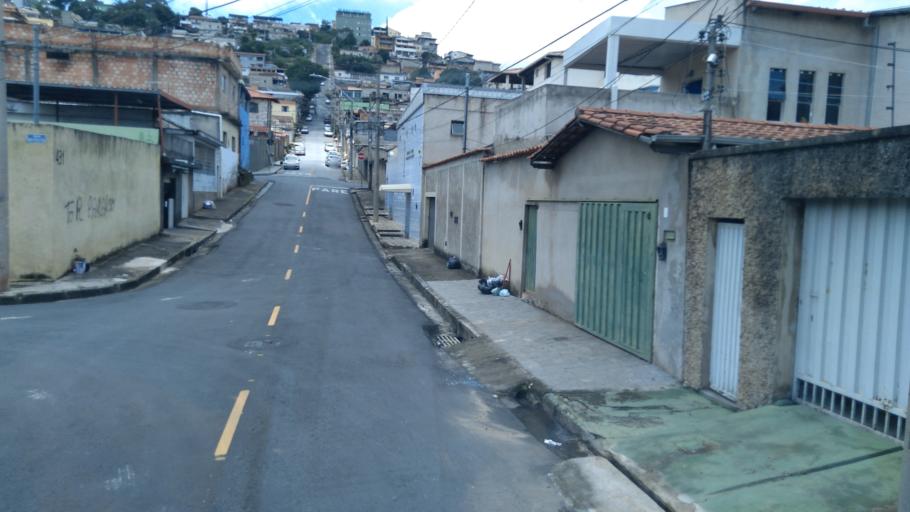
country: BR
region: Minas Gerais
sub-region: Belo Horizonte
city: Belo Horizonte
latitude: -19.9221
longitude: -43.9031
